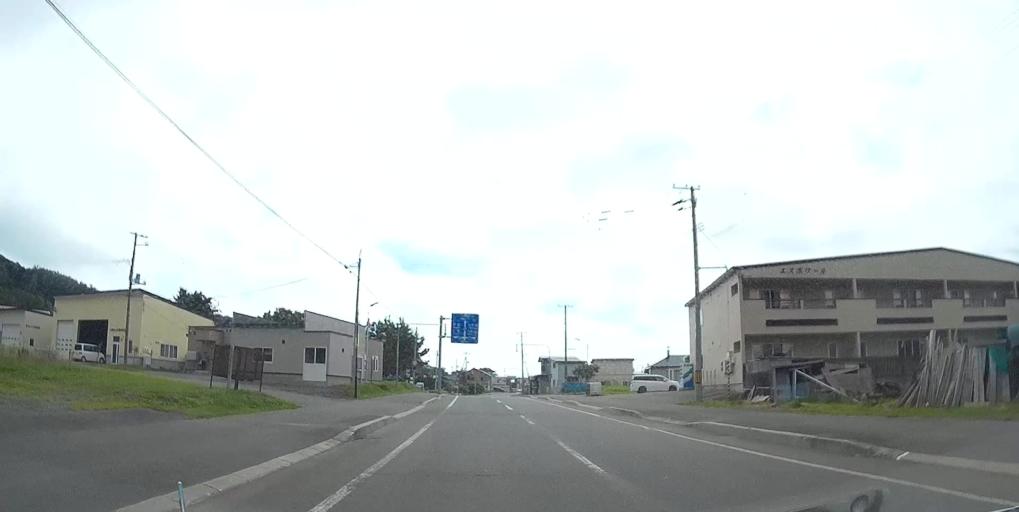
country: JP
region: Hokkaido
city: Kamiiso
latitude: 41.9709
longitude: 140.1413
